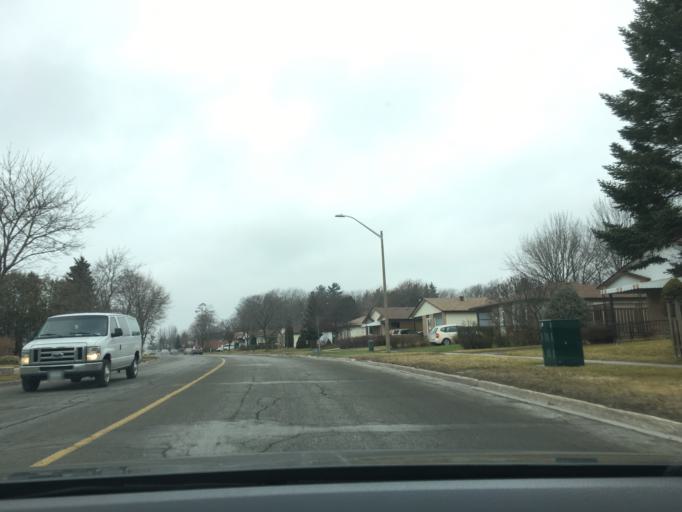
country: CA
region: Ontario
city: Barrie
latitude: 44.3950
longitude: -79.7229
